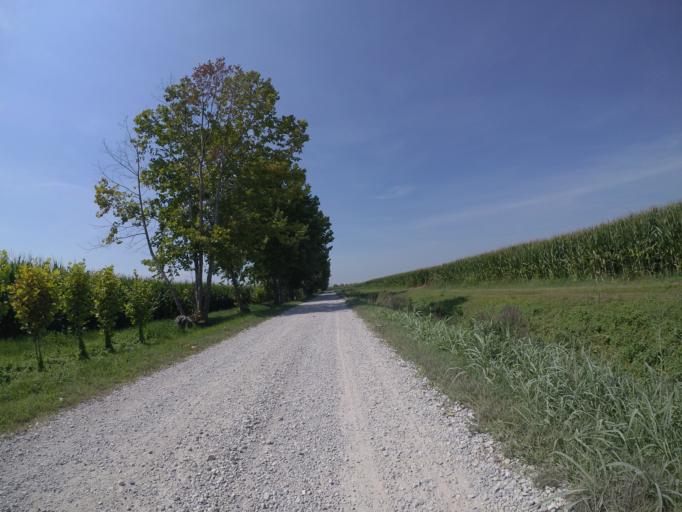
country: IT
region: Friuli Venezia Giulia
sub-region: Provincia di Udine
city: Varmo
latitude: 45.9150
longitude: 12.9914
